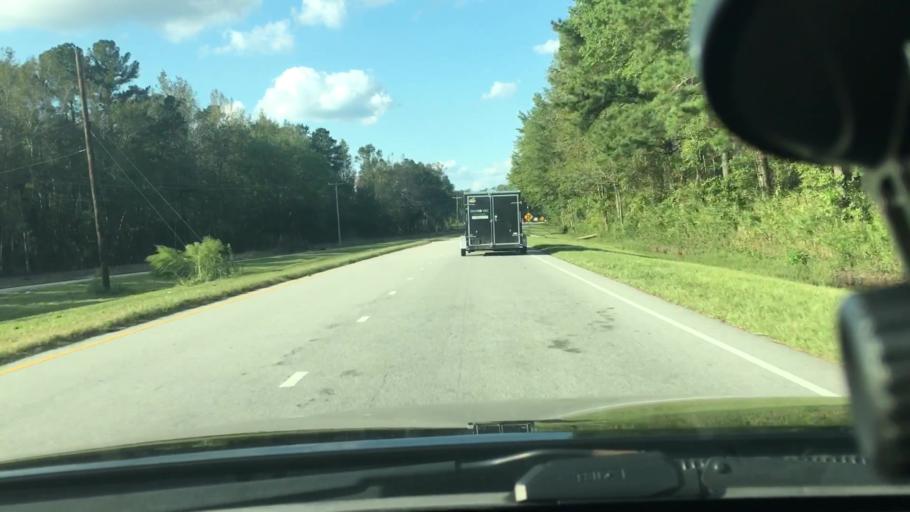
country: US
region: North Carolina
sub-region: Craven County
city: Vanceboro
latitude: 35.3348
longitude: -77.1510
